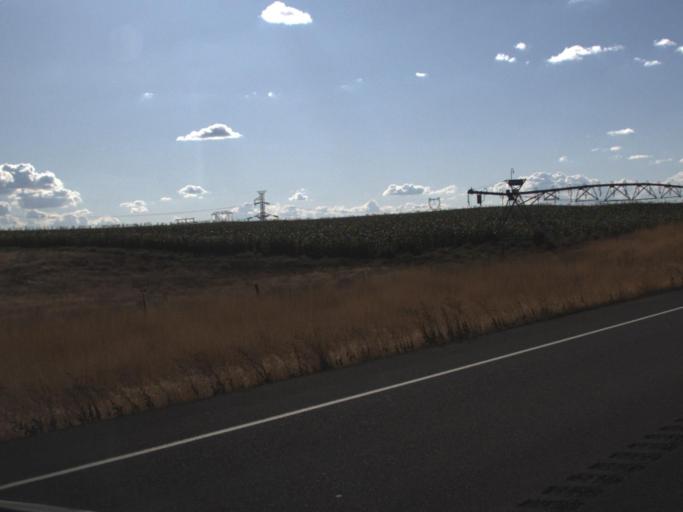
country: US
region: Oregon
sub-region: Umatilla County
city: Umatilla
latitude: 45.9475
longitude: -119.3820
